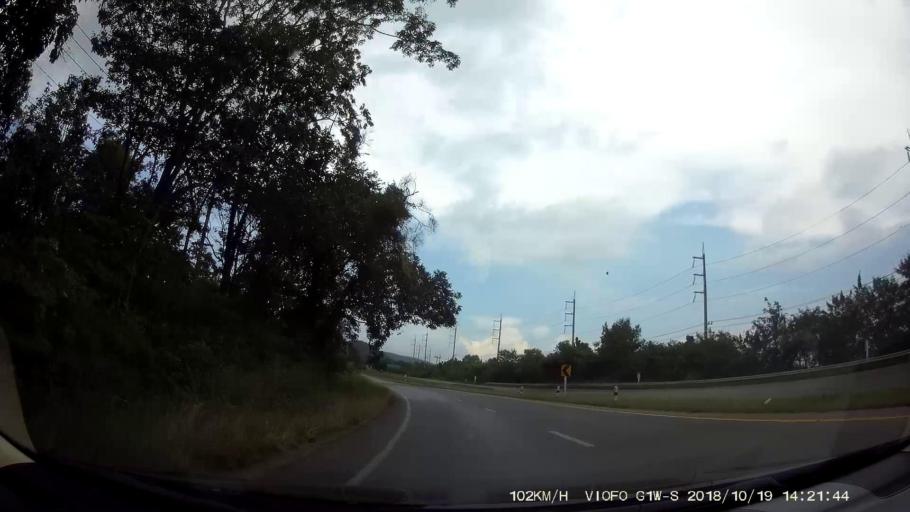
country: TH
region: Chaiyaphum
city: Kaeng Khro
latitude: 16.0553
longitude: 102.2697
